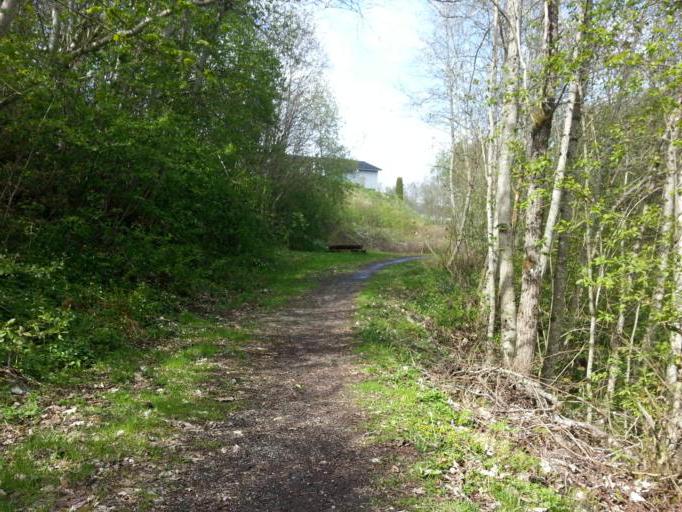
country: NO
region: Sor-Trondelag
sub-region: Trondheim
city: Trondheim
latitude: 63.3877
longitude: 10.3597
